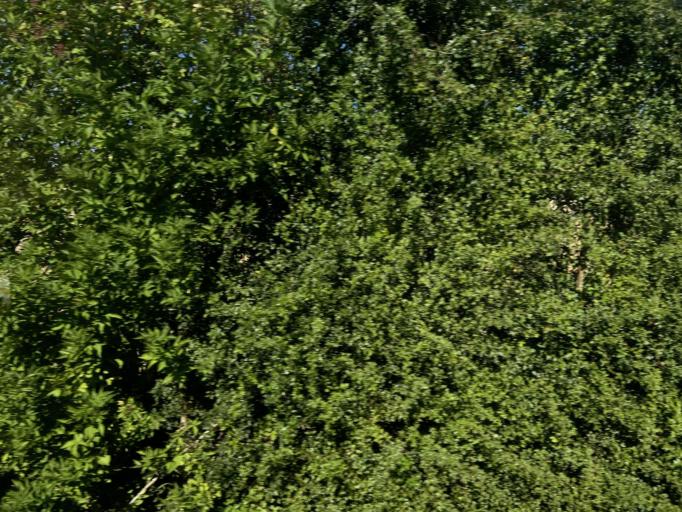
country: GB
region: England
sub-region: Lincolnshire
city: Spilsby
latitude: 53.0649
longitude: 0.0649
